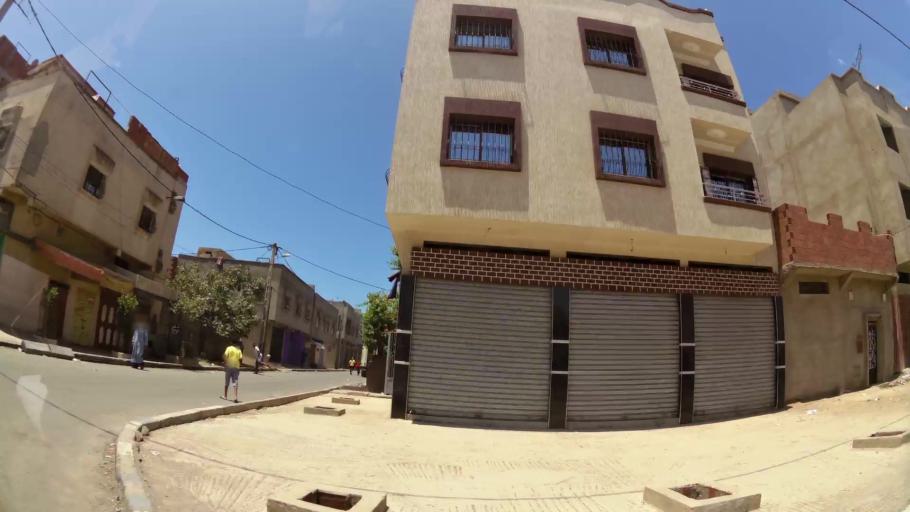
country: MA
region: Gharb-Chrarda-Beni Hssen
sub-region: Kenitra Province
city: Kenitra
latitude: 34.2586
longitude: -6.6488
